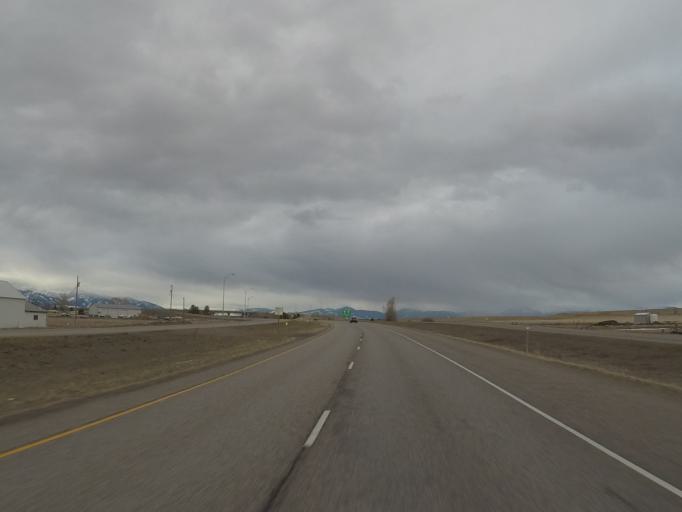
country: US
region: Montana
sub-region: Gallatin County
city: Manhattan
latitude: 45.8532
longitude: -111.3455
